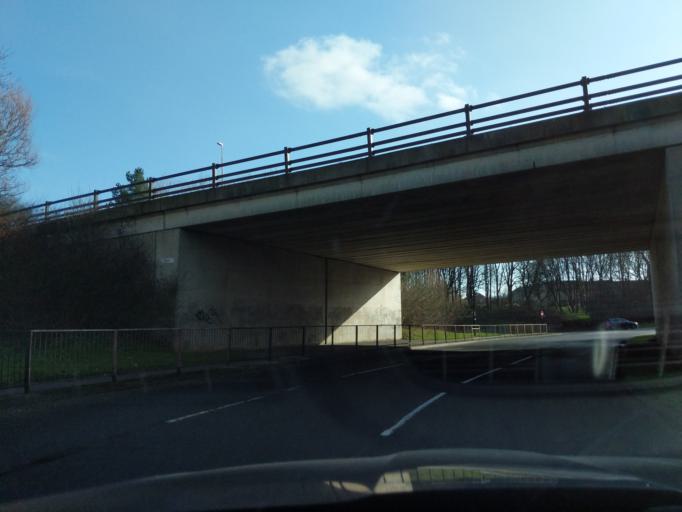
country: GB
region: England
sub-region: Sunderland
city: Washington
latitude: 54.9057
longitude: -1.5284
